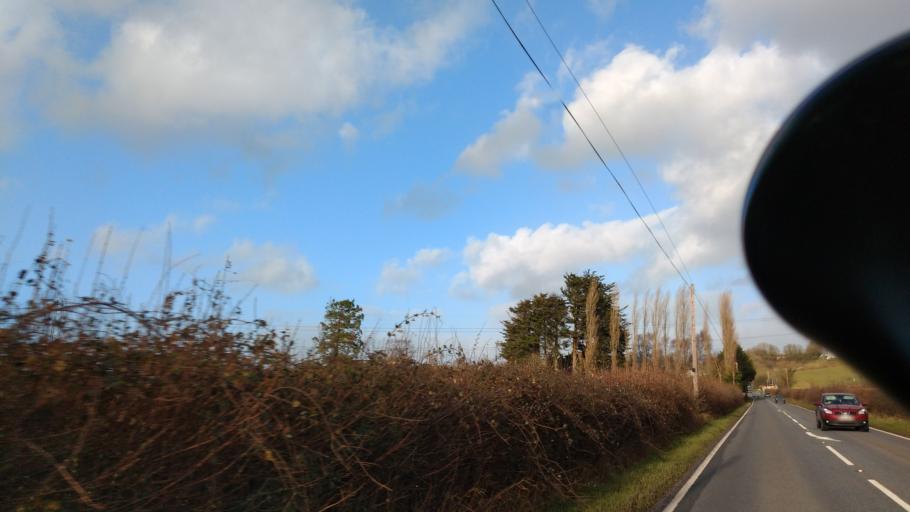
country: GB
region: England
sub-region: Somerset
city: Shepton Mallet
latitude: 51.1583
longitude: -2.5419
